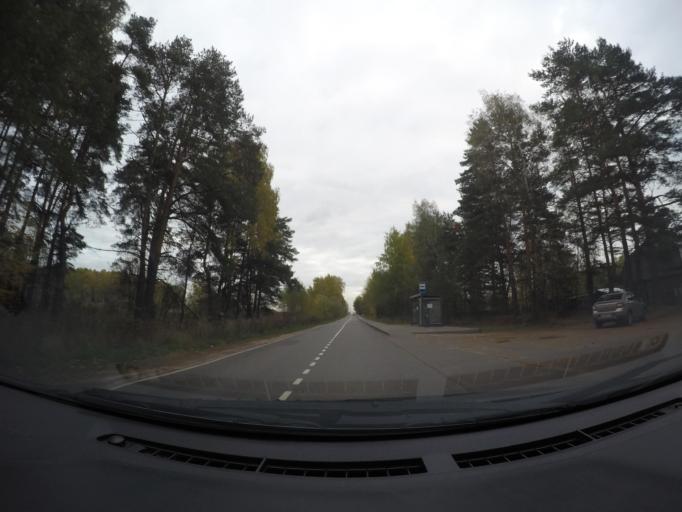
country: RU
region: Moskovskaya
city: Vishnyakovskiye Dachi
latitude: 55.8058
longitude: 38.1260
